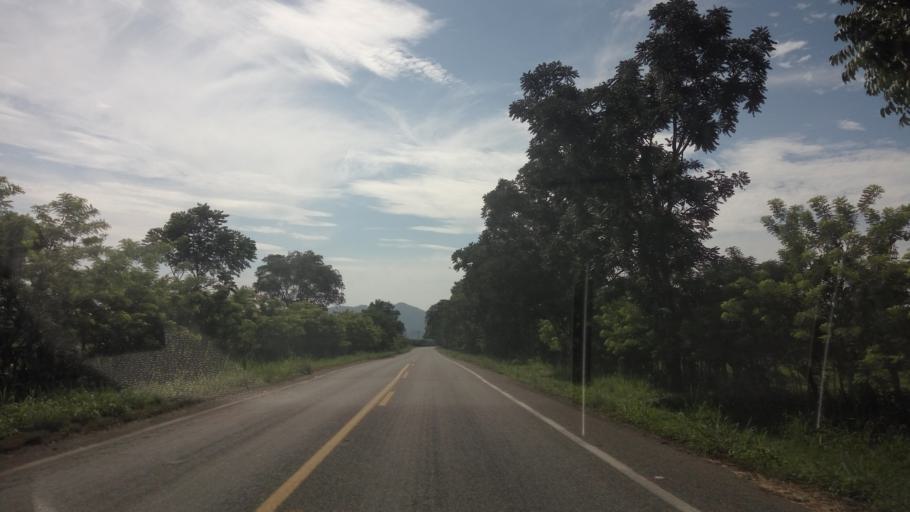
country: MX
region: Tabasco
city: Teapa
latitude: 17.6034
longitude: -92.9661
